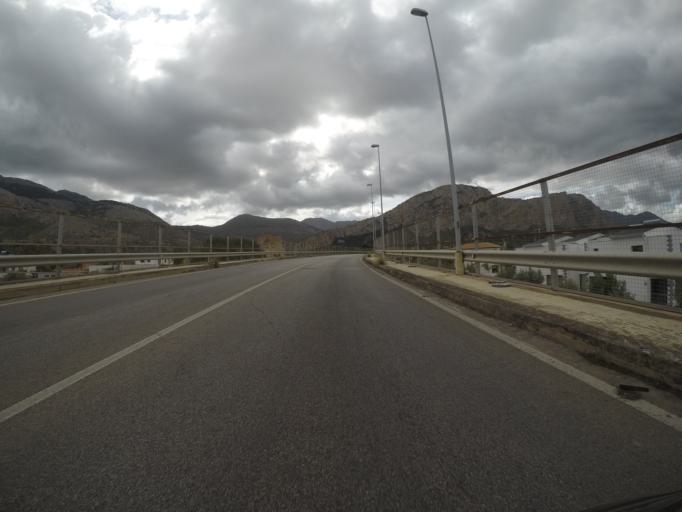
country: IT
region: Sicily
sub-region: Palermo
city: Capaci
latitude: 38.1683
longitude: 13.2217
